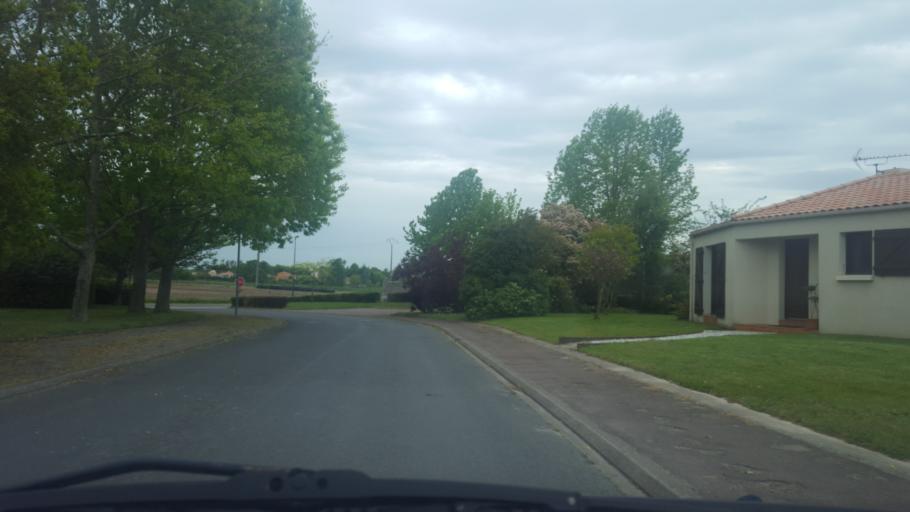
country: FR
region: Pays de la Loire
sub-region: Departement de la Loire-Atlantique
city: Montbert
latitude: 47.0572
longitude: -1.4825
